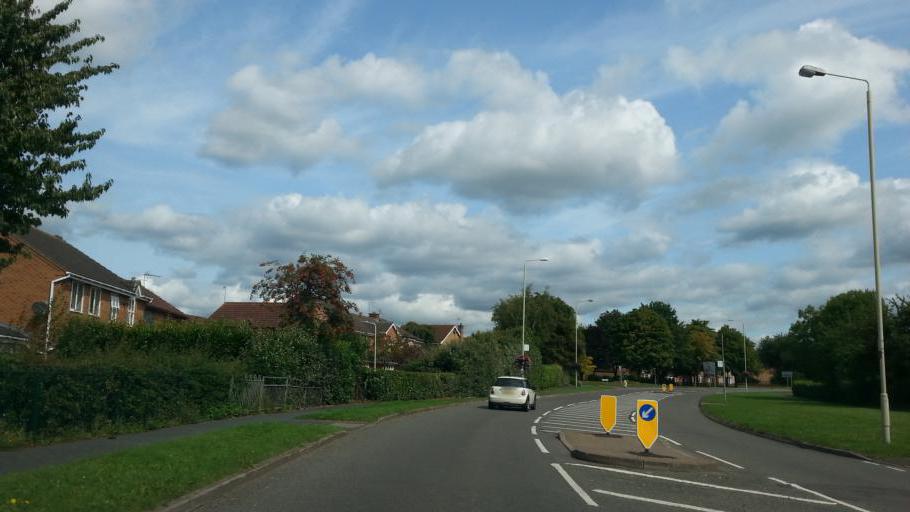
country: GB
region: England
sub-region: Leicestershire
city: Blaby
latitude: 52.5606
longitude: -1.1735
